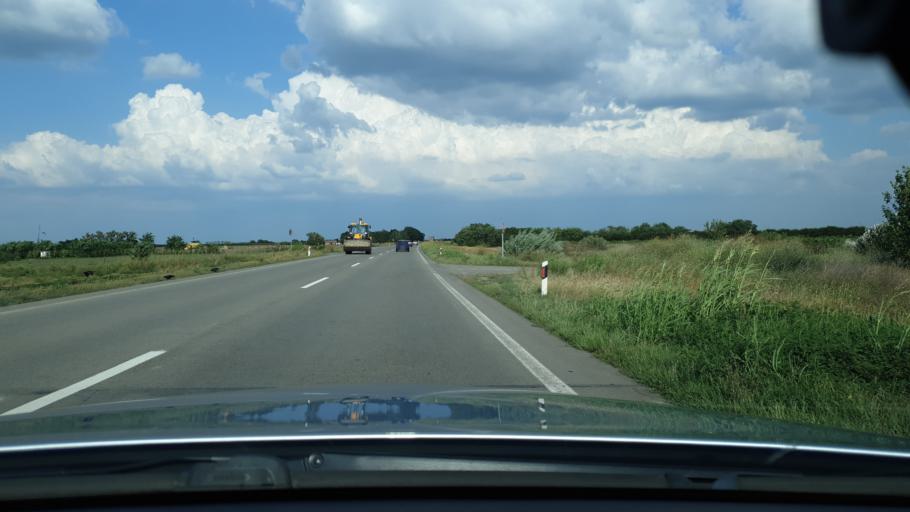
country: RS
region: Autonomna Pokrajina Vojvodina
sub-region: Juznobacki Okrug
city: Zabalj
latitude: 45.3624
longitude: 20.0897
